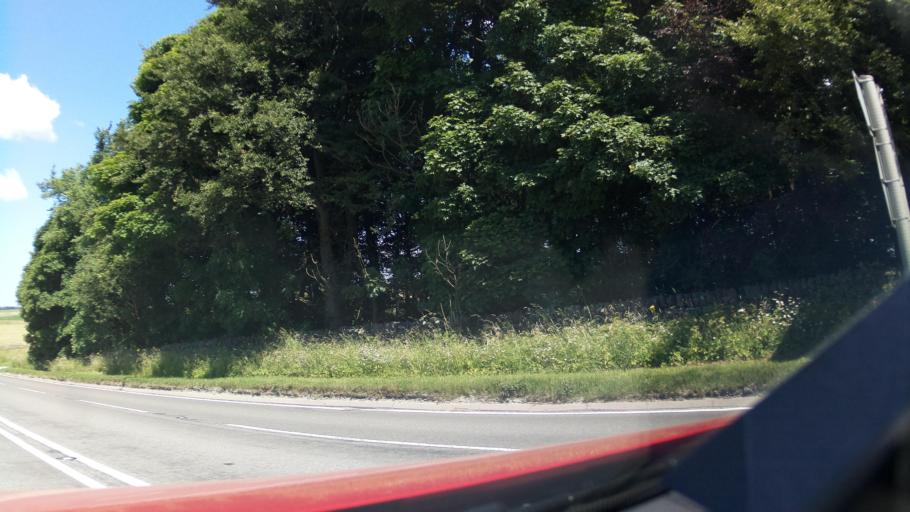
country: GB
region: England
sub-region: Derbyshire
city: Buxton
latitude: 53.2252
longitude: -1.8719
